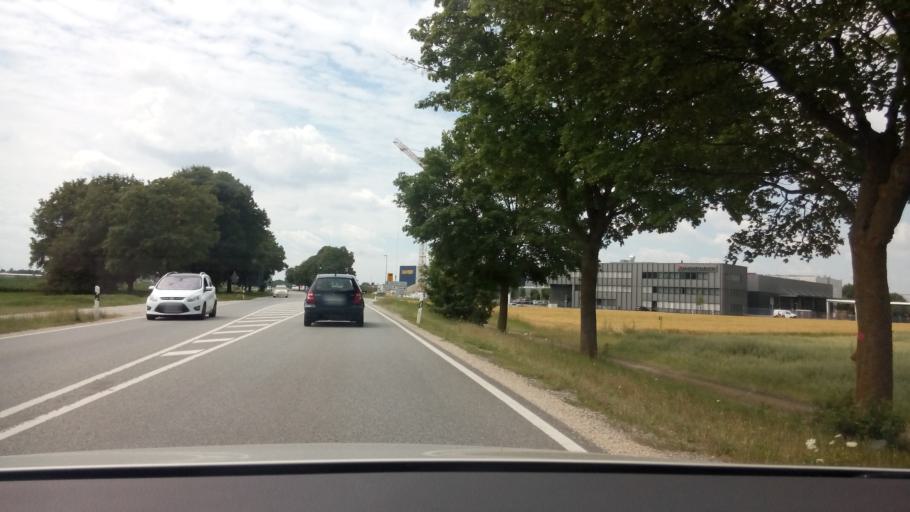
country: DE
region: Bavaria
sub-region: Upper Bavaria
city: Neufahrn bei Freising
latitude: 48.3310
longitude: 11.6962
